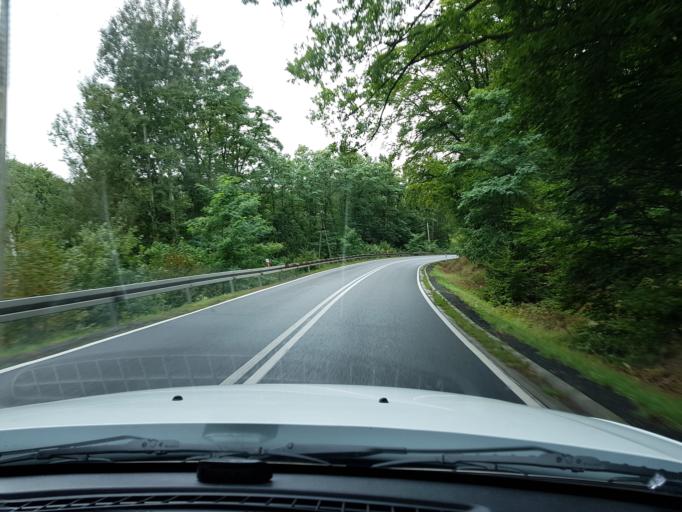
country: PL
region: West Pomeranian Voivodeship
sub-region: Powiat gryfinski
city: Widuchowa
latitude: 53.0901
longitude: 14.4249
